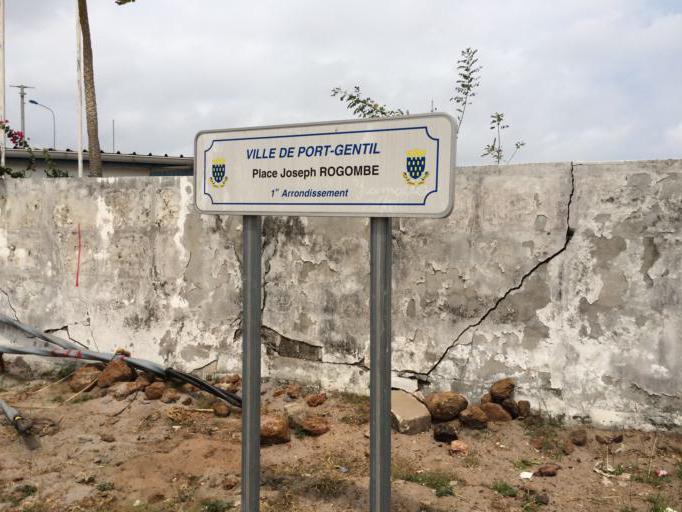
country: GA
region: Ogooue-Maritime
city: Port-Gentil
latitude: -0.7046
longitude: 8.7725
